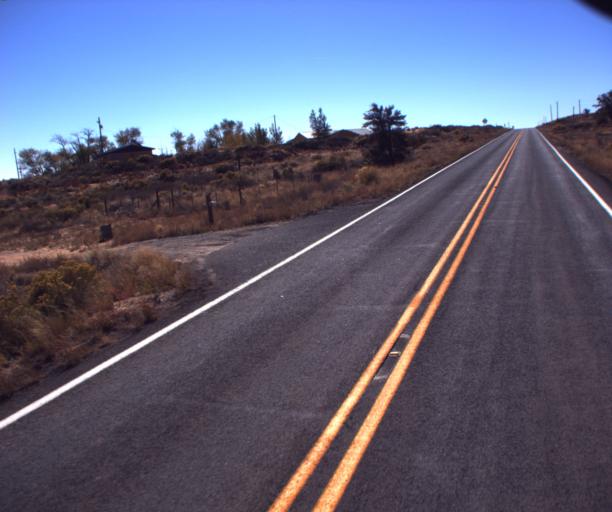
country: US
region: Arizona
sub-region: Navajo County
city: First Mesa
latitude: 35.9204
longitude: -110.6634
